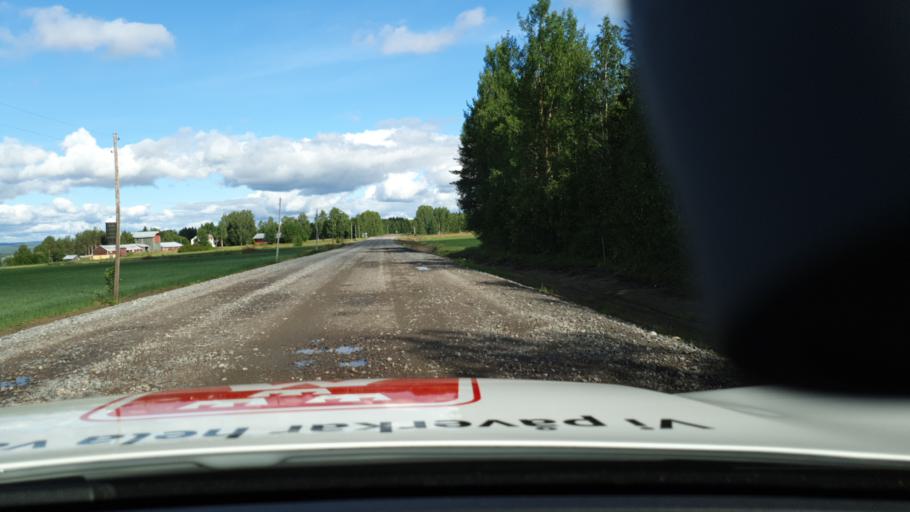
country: SE
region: Norrbotten
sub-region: Bodens Kommun
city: Boden
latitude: 65.8846
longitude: 21.3965
